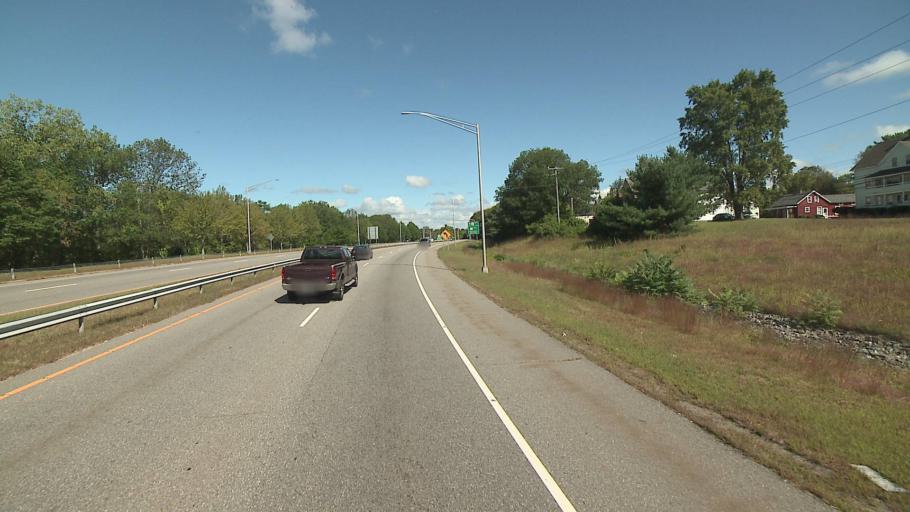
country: US
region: Connecticut
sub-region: Windham County
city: Danielson
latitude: 41.7980
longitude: -71.8852
